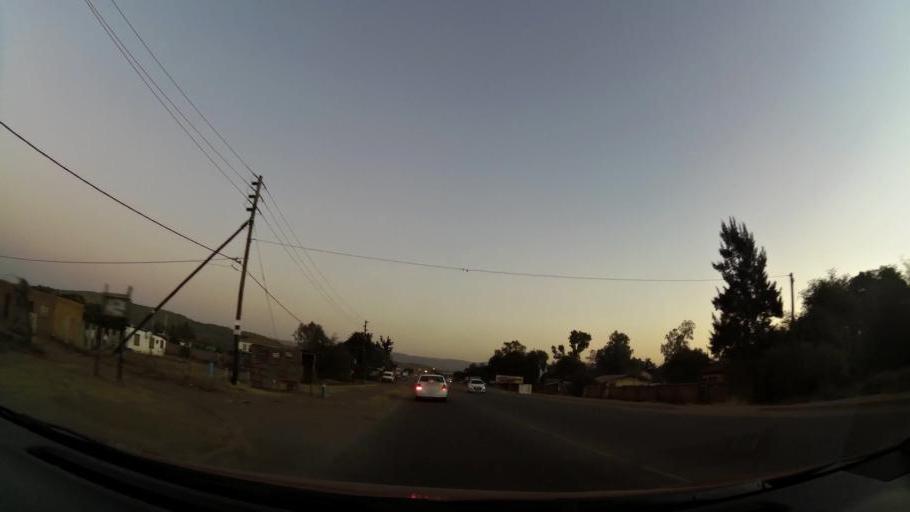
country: ZA
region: North-West
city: Ga-Rankuwa
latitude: -25.6151
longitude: 27.9633
